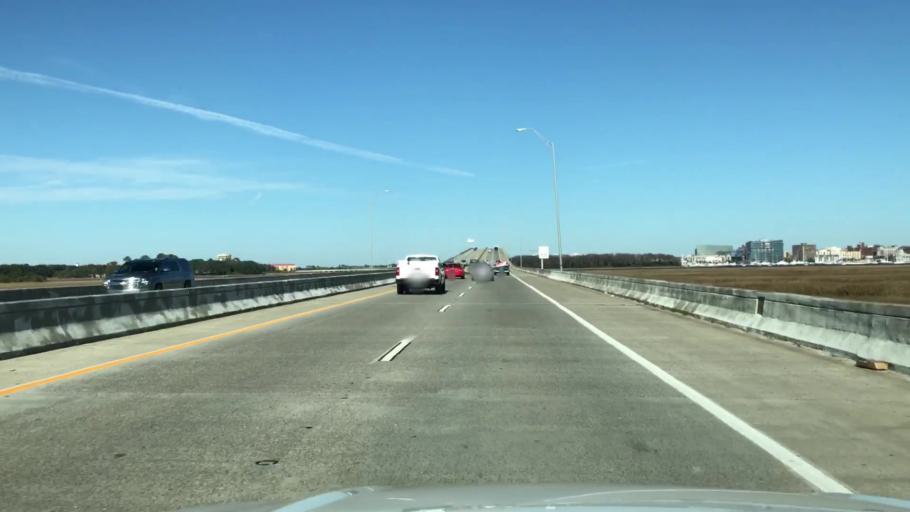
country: US
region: South Carolina
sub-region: Charleston County
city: Charleston
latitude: 32.7626
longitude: -79.9580
